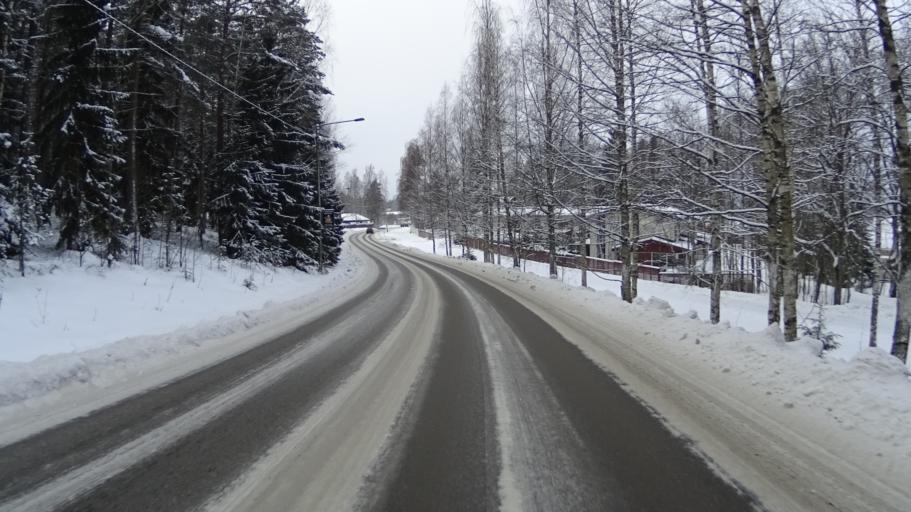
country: FI
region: Uusimaa
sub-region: Helsinki
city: Vihti
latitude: 60.3418
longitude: 24.3009
